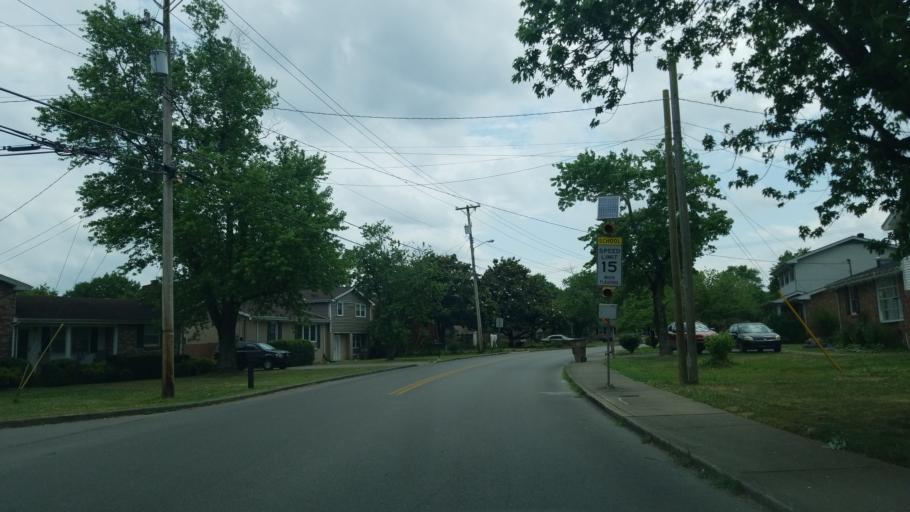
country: US
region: Tennessee
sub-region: Rutherford County
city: La Vergne
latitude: 36.0812
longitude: -86.6237
